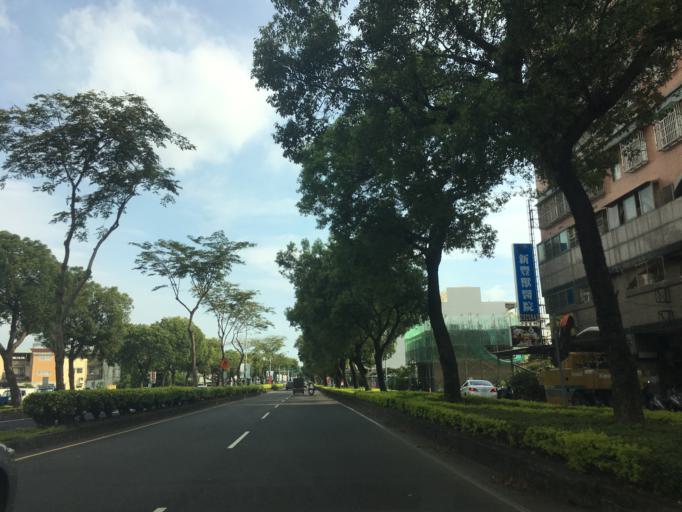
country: TW
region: Taiwan
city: Zhongxing New Village
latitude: 23.9829
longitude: 120.6815
